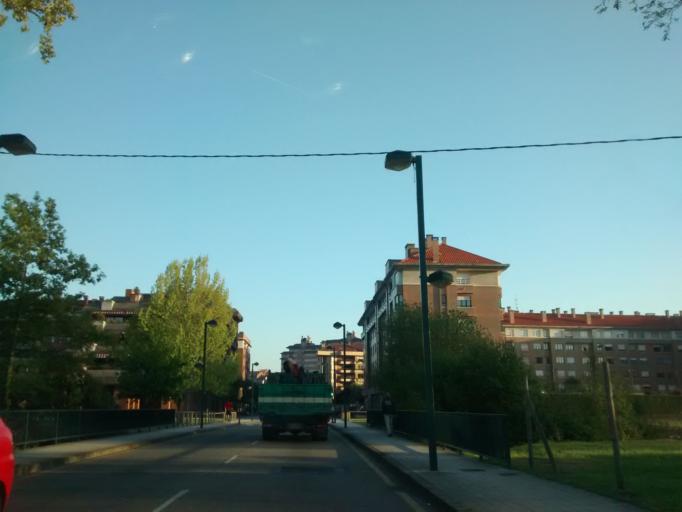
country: ES
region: Asturias
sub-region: Province of Asturias
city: Gijon
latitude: 43.5263
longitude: -5.6425
